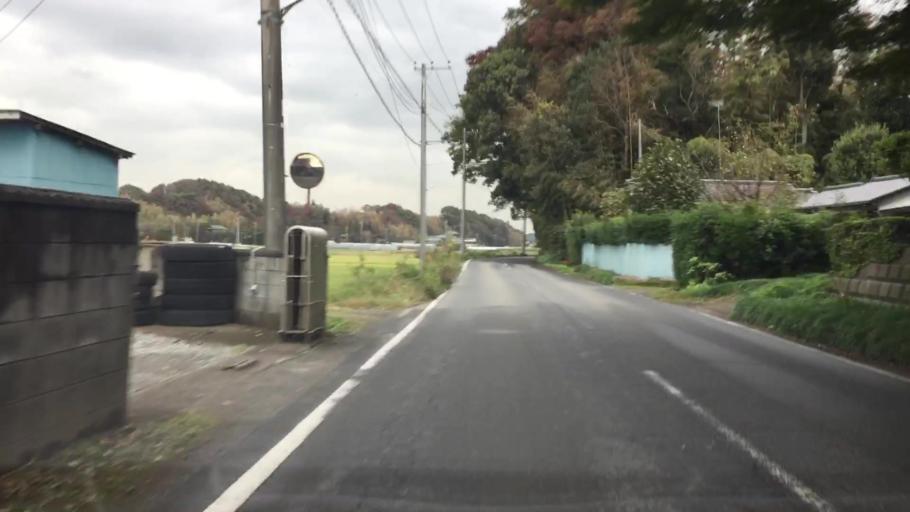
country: JP
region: Chiba
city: Abiko
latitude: 35.8407
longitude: 140.0420
